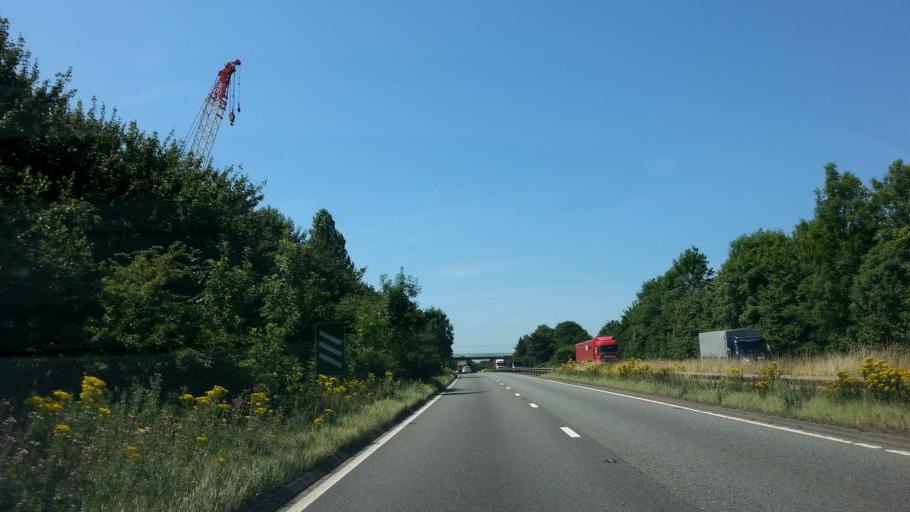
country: GB
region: England
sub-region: Derbyshire
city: Alfreton
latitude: 53.0921
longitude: -1.3656
